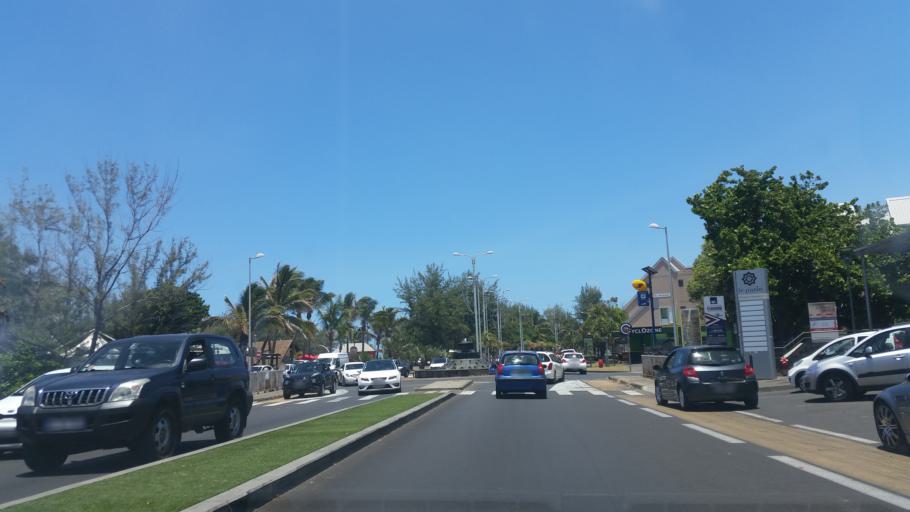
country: RE
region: Reunion
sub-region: Reunion
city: Saint-Pierre
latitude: -21.3408
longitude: 55.4615
